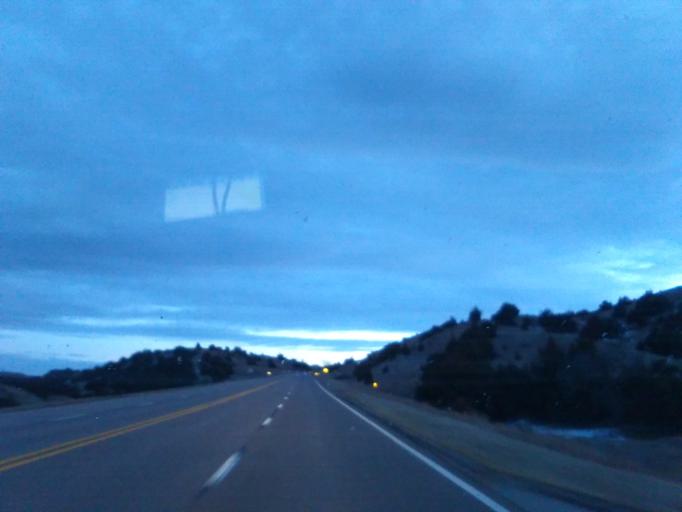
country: US
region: Nebraska
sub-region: Garden County
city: Oshkosh
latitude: 41.2644
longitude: -102.1100
